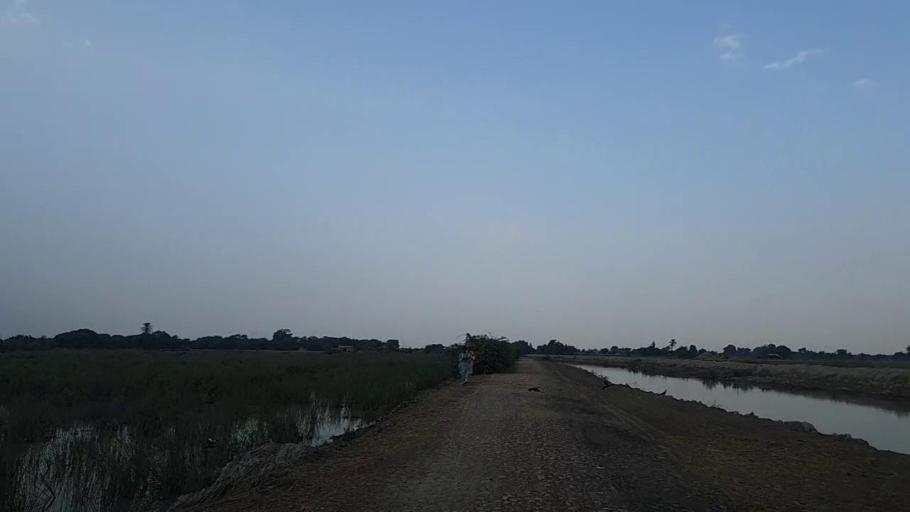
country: PK
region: Sindh
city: Daro Mehar
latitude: 24.7608
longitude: 68.1359
